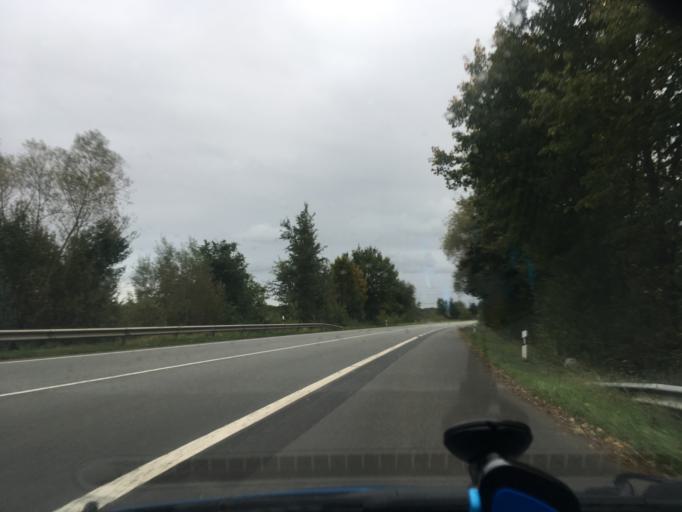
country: DE
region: Lower Saxony
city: Handorf
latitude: 53.3808
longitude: 10.3473
